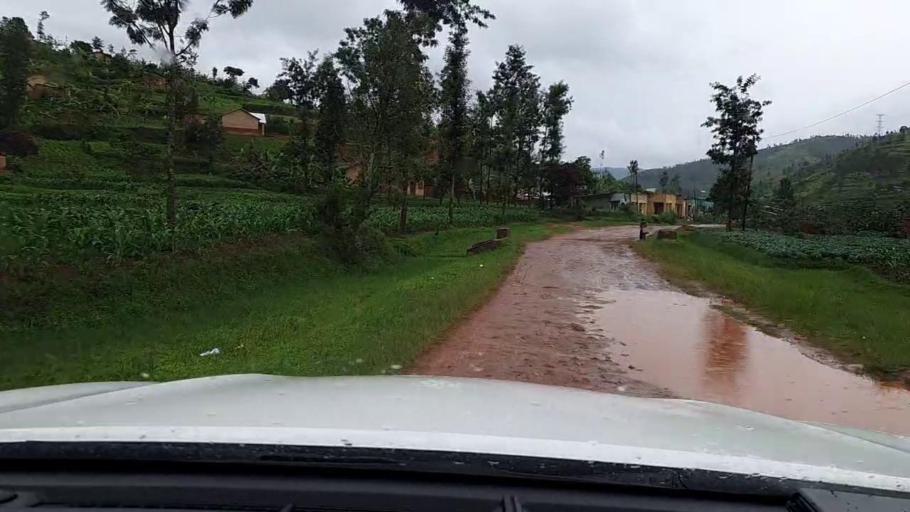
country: RW
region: Northern Province
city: Byumba
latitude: -1.7444
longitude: 29.9451
